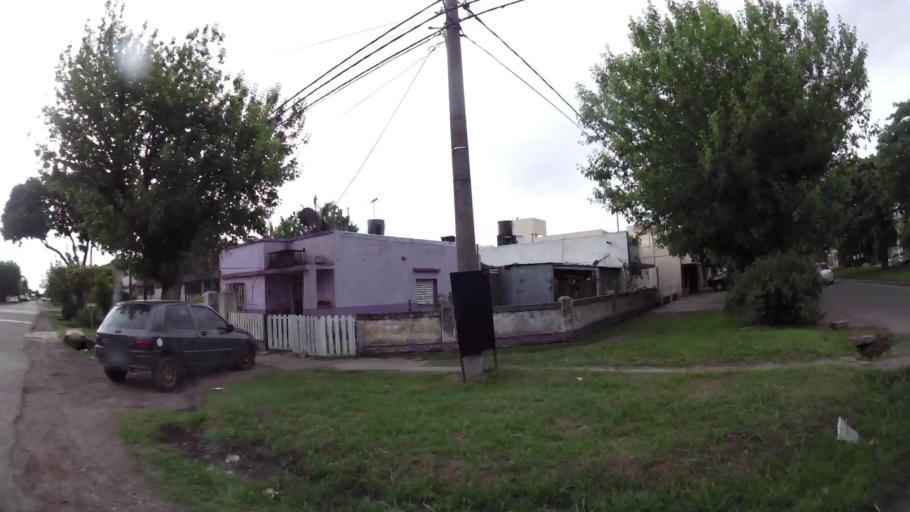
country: AR
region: Santa Fe
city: Gobernador Galvez
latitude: -33.0039
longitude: -60.6778
